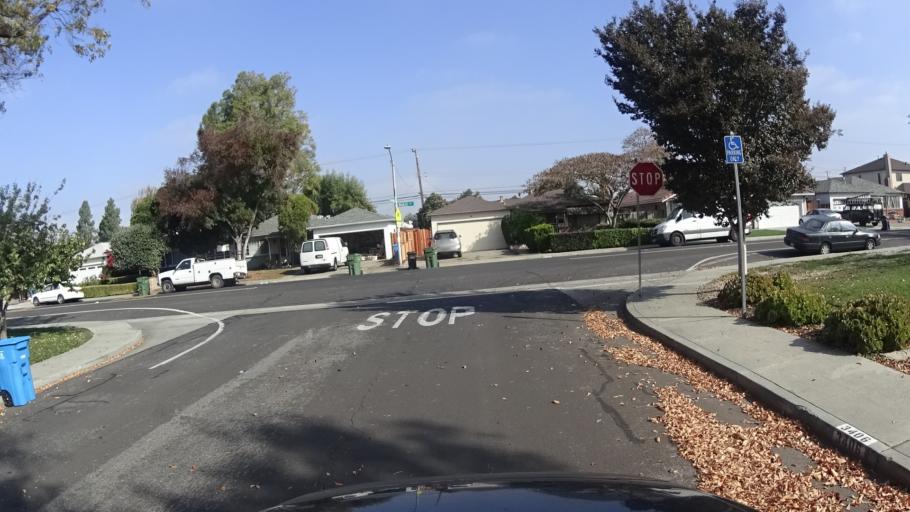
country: US
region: California
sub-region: Santa Clara County
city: Santa Clara
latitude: 37.3576
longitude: -121.9898
